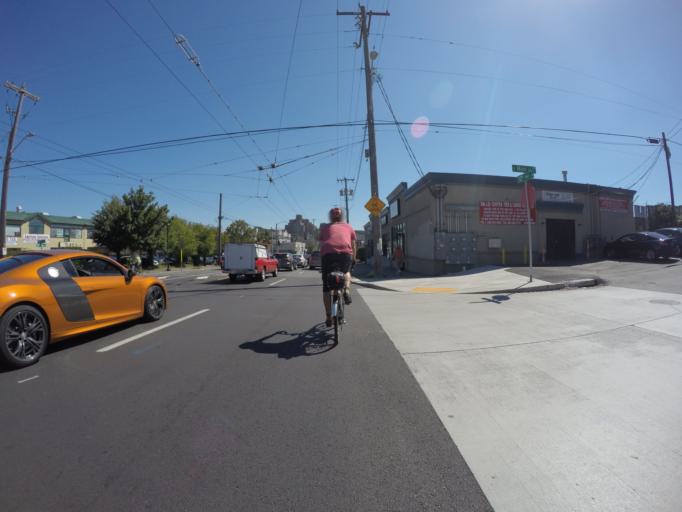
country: US
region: Washington
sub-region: King County
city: Seattle
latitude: 47.6001
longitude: -122.3172
